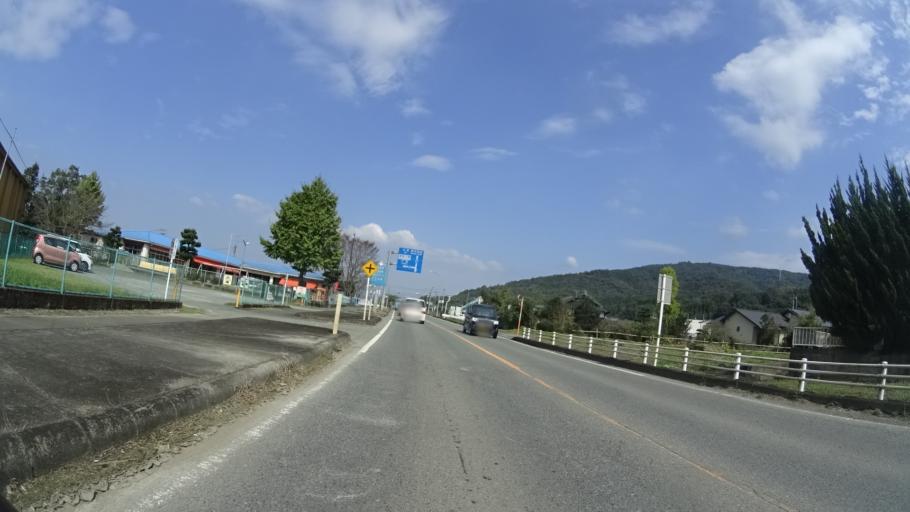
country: JP
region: Kumamoto
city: Ozu
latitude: 32.7583
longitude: 130.8121
